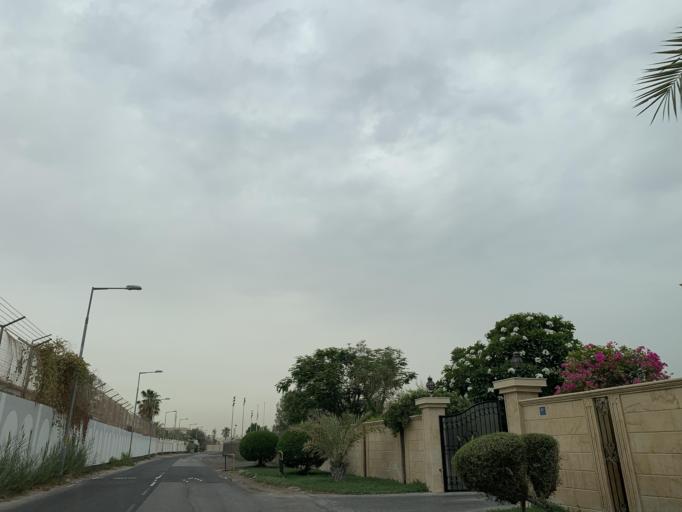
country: BH
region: Northern
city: Madinat `Isa
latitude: 26.1943
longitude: 50.4712
